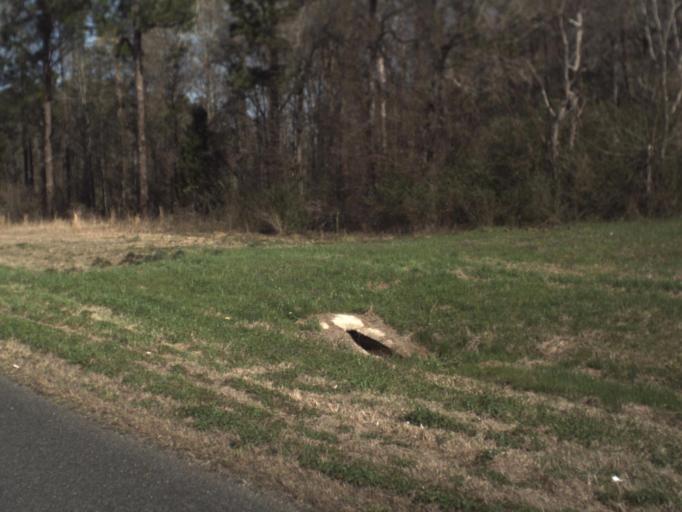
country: US
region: Florida
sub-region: Jackson County
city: Graceville
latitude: 30.9750
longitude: -85.4093
